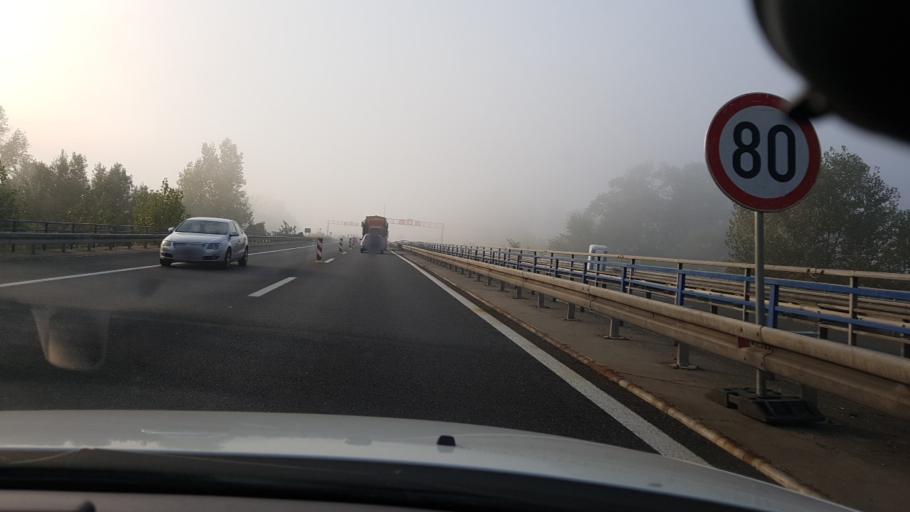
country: HR
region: Zagrebacka
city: Bestovje
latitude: 45.8262
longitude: 15.8200
